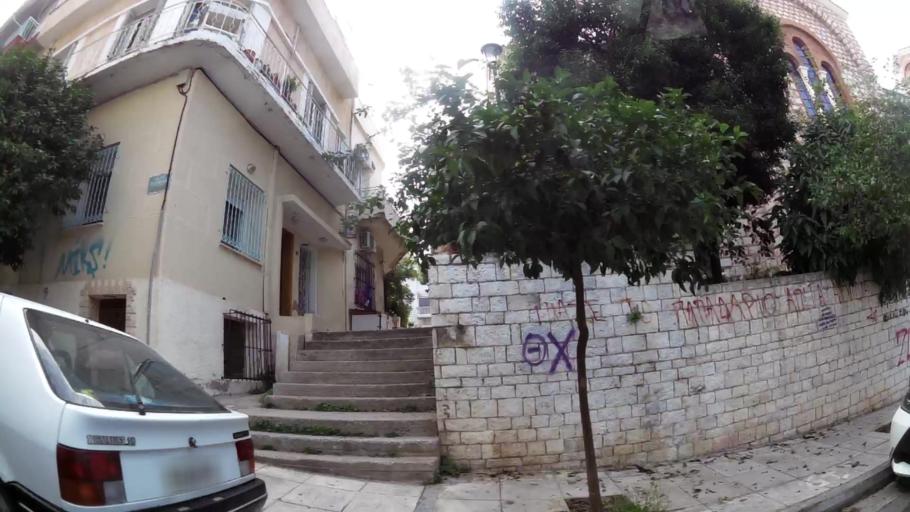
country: GR
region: Attica
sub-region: Nomarchia Athinas
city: Athens
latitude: 37.9709
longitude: 23.7126
